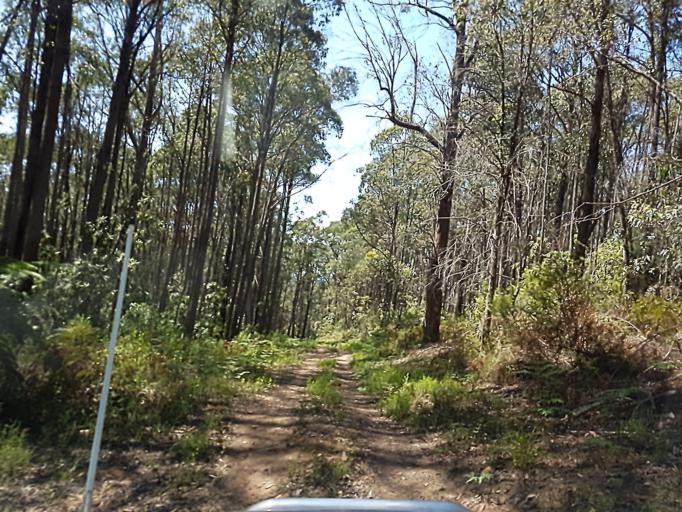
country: AU
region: Victoria
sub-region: East Gippsland
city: Lakes Entrance
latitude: -37.3132
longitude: 148.3334
